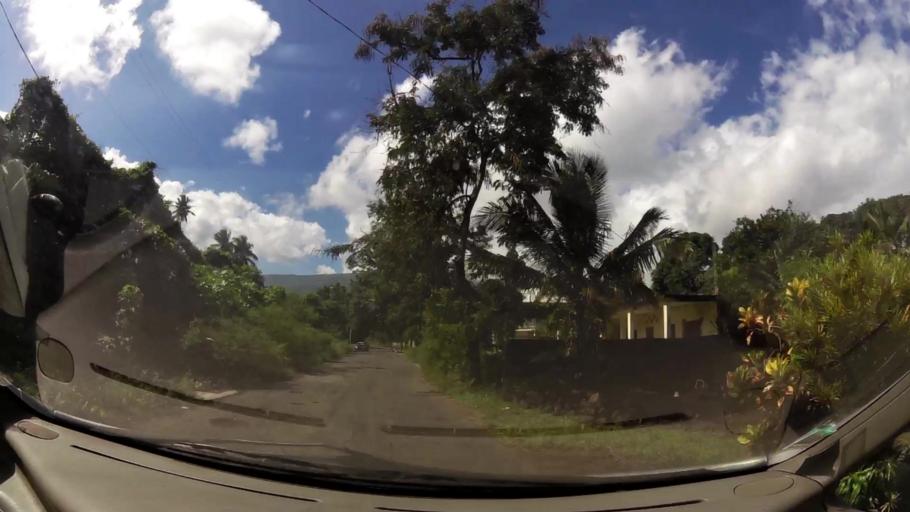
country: KM
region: Grande Comore
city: Mavingouni
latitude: -11.7409
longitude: 43.2442
